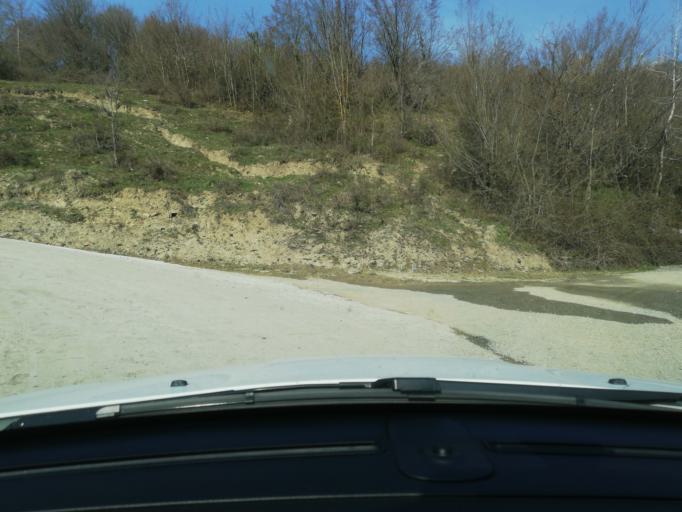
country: TR
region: Karabuk
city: Yenice
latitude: 41.2634
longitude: 32.3615
